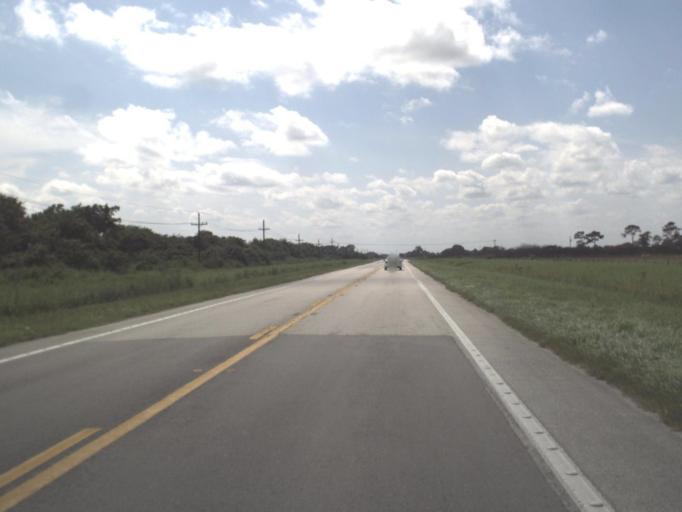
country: US
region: Florida
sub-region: Hendry County
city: Port LaBelle
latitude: 26.6508
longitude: -81.4362
